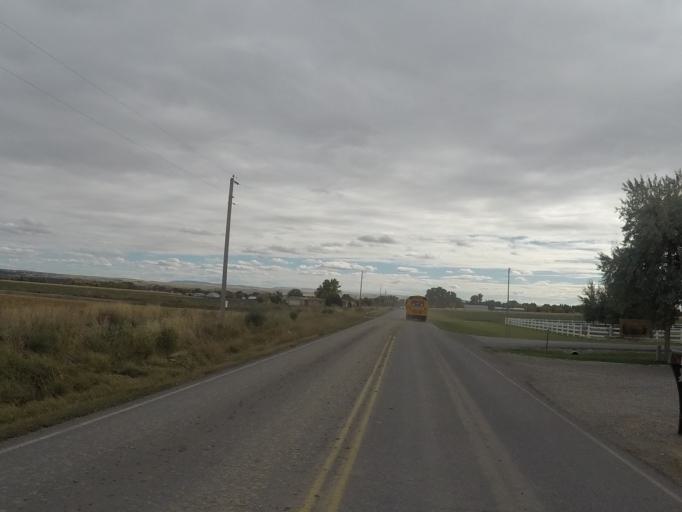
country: US
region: Montana
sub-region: Yellowstone County
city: Laurel
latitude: 45.7475
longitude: -108.6589
